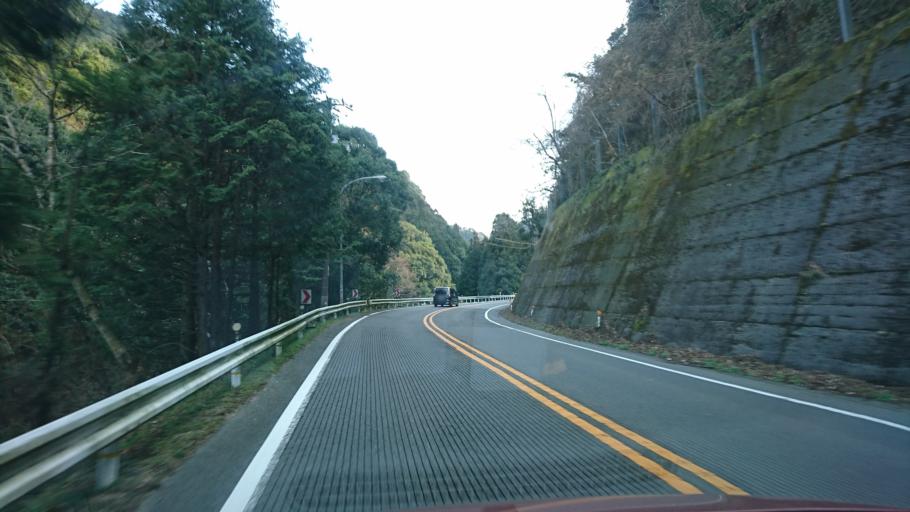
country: JP
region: Ehime
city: Hojo
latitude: 33.9632
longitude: 132.9069
